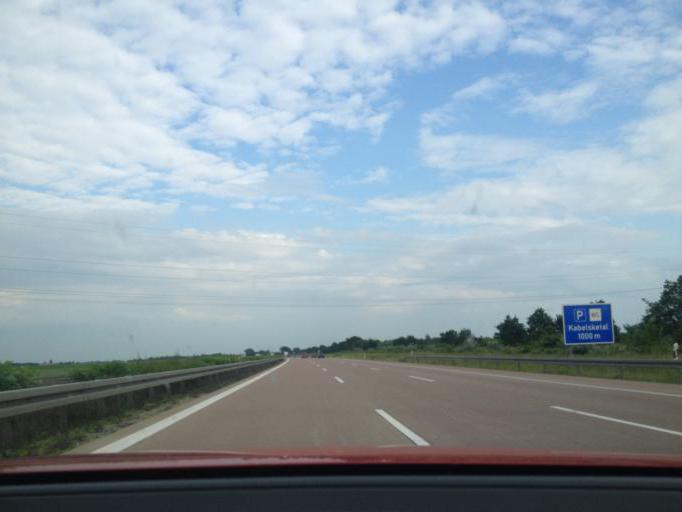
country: DE
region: Saxony-Anhalt
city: Dolbau
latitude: 51.4643
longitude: 12.0944
